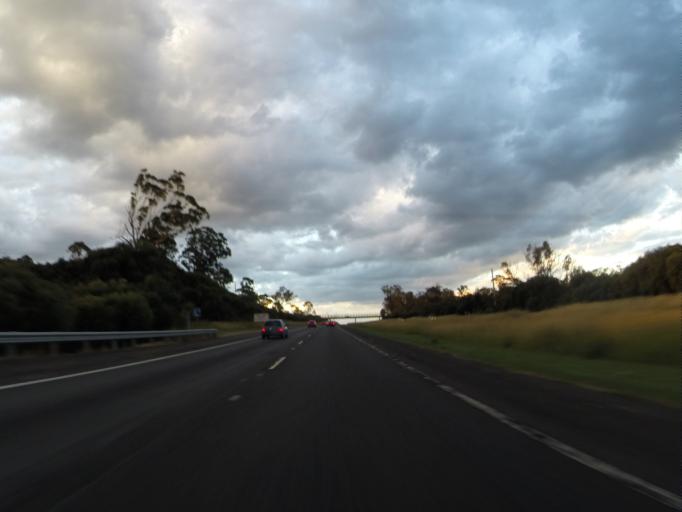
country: AU
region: New South Wales
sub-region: Campbelltown Municipality
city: Glen Alpine
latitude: -34.0908
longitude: 150.7669
